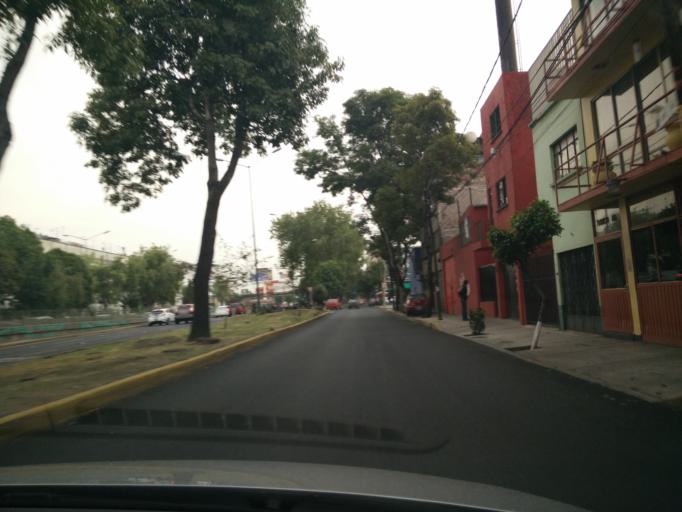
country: MX
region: Mexico City
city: Benito Juarez
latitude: 19.4039
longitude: -99.1493
